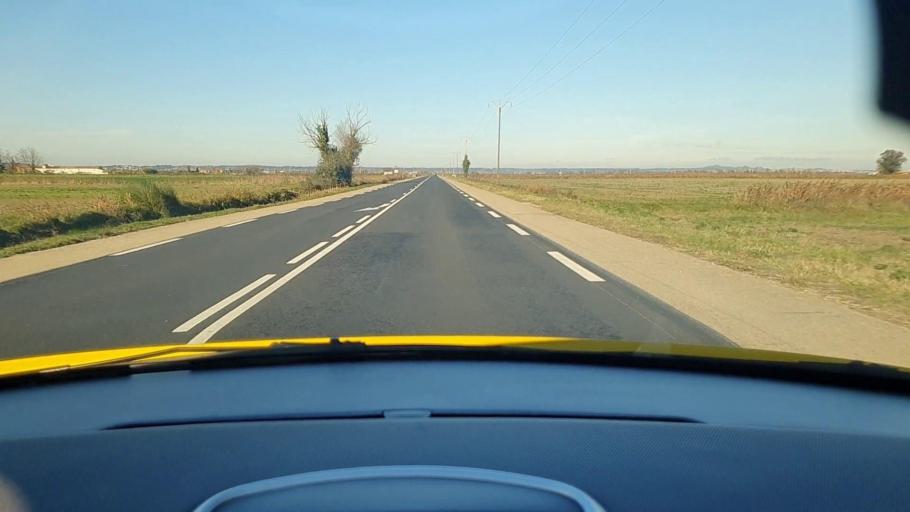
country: FR
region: Languedoc-Roussillon
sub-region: Departement du Gard
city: Bellegarde
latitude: 43.7127
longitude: 4.5489
